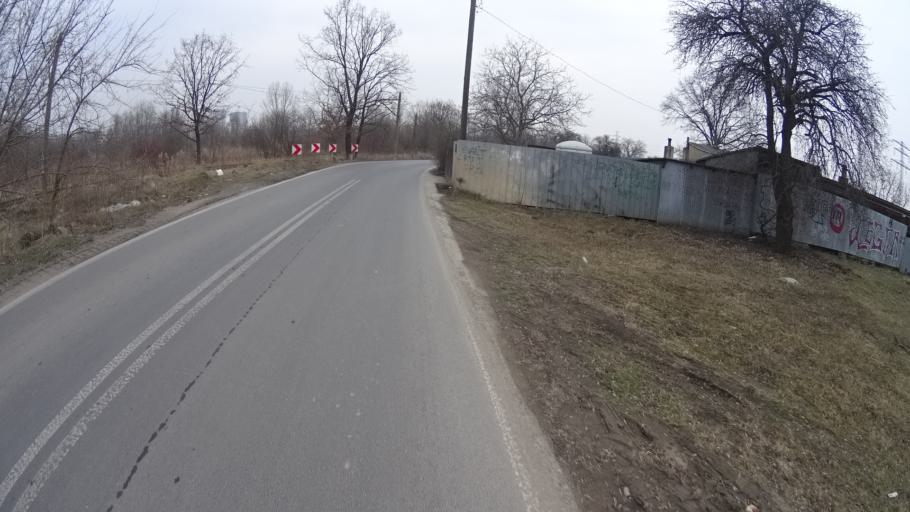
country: PL
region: Masovian Voivodeship
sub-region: Warszawa
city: Wlochy
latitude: 52.2199
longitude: 20.9432
